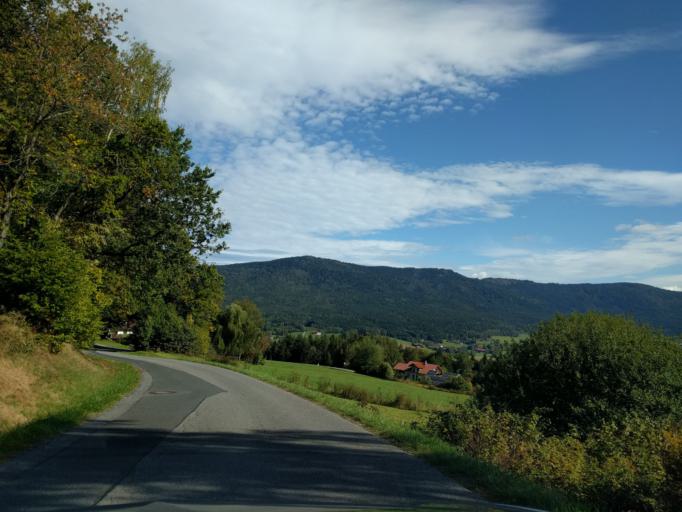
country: DE
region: Bavaria
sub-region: Upper Palatinate
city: Kotzting
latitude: 49.1476
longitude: 12.8881
